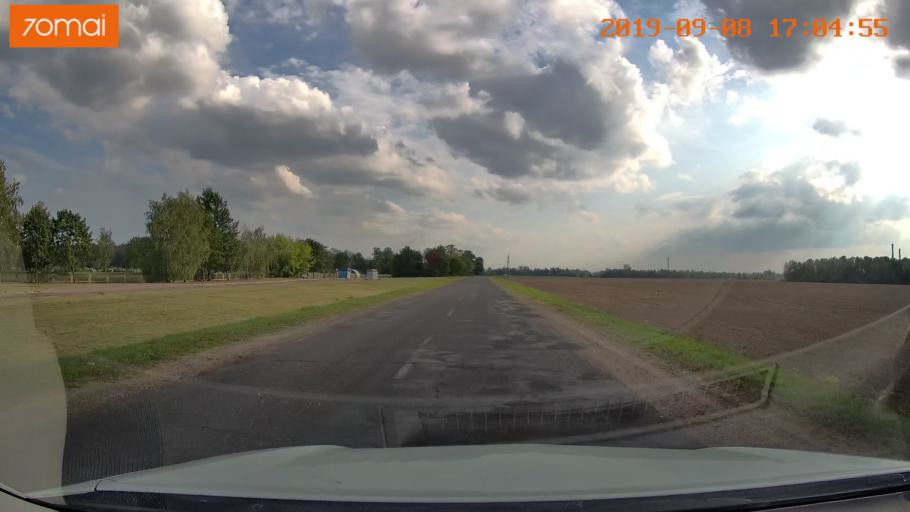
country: BY
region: Grodnenskaya
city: Hrodna
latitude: 53.6846
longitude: 23.9557
